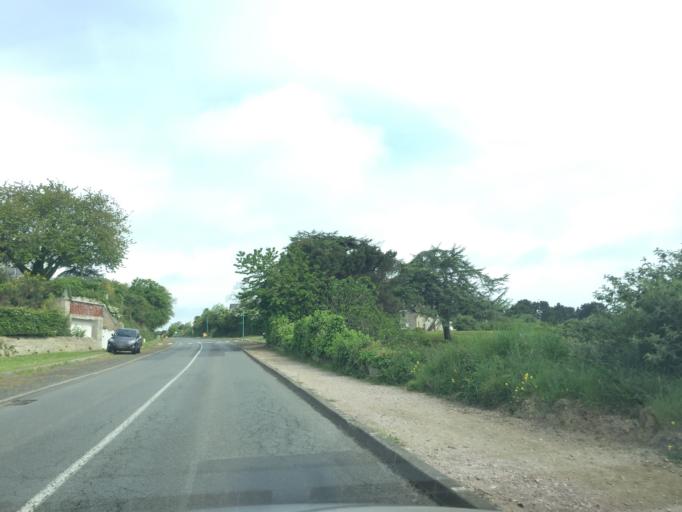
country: FR
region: Brittany
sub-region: Departement des Cotes-d'Armor
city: Saint-Cast-le-Guildo
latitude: 48.6150
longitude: -2.2459
